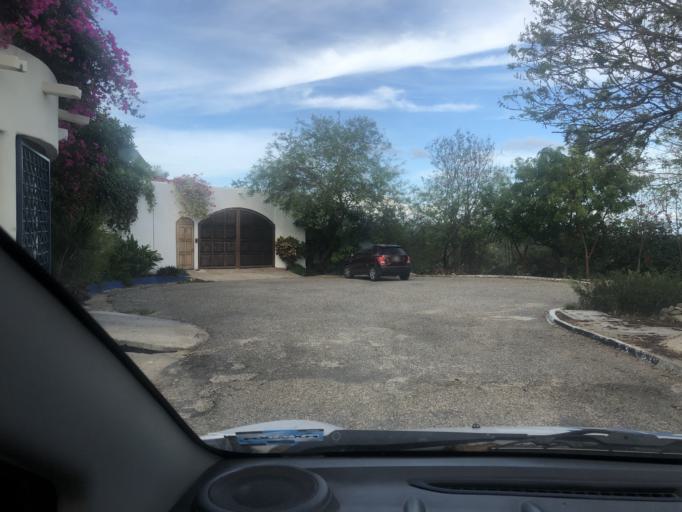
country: MX
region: Oaxaca
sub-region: Santa Maria Huatulco
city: Crucecita
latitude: 15.7715
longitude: -96.0862
